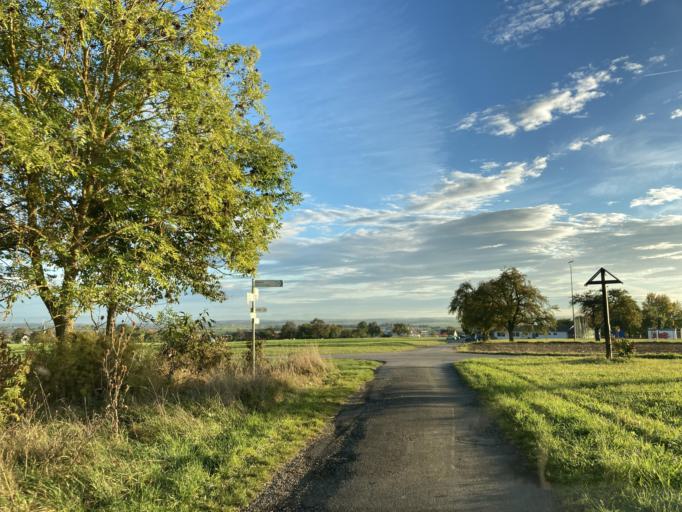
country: DE
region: Baden-Wuerttemberg
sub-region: Regierungsbezirk Stuttgart
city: Motzingen
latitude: 48.5118
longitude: 8.7694
